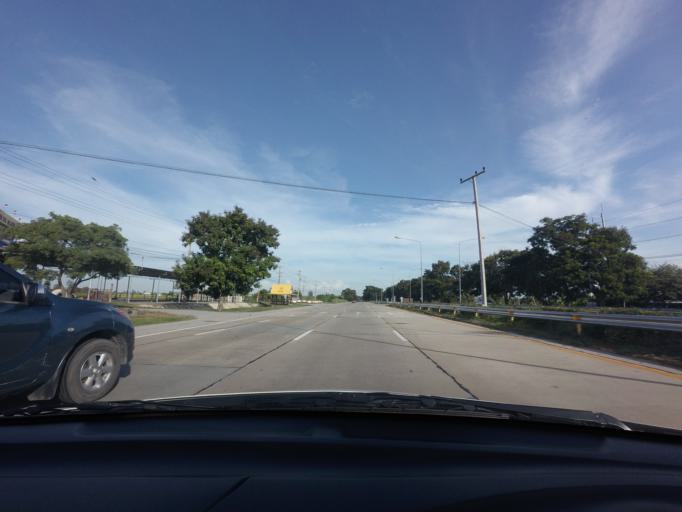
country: TH
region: Phra Nakhon Si Ayutthaya
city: Lat Bua Luang
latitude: 14.2168
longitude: 100.2827
